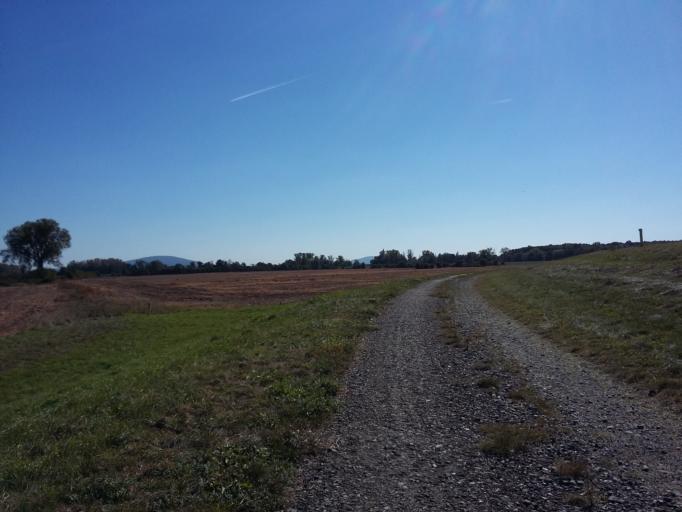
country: AT
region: Lower Austria
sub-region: Politischer Bezirk Ganserndorf
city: Marchegg
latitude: 48.3069
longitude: 16.9251
